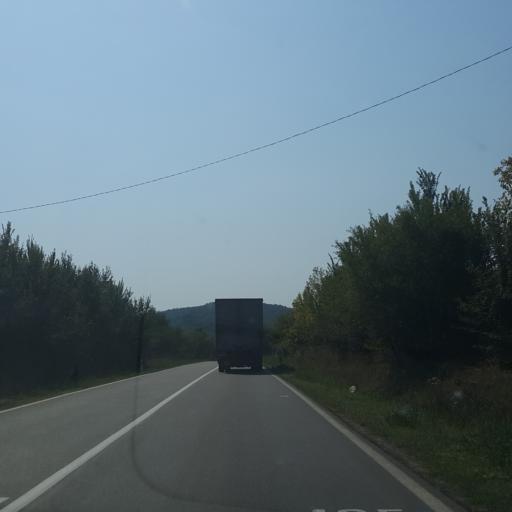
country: RS
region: Central Serbia
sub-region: Zajecarski Okrug
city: Zajecar
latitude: 43.8225
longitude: 22.2876
